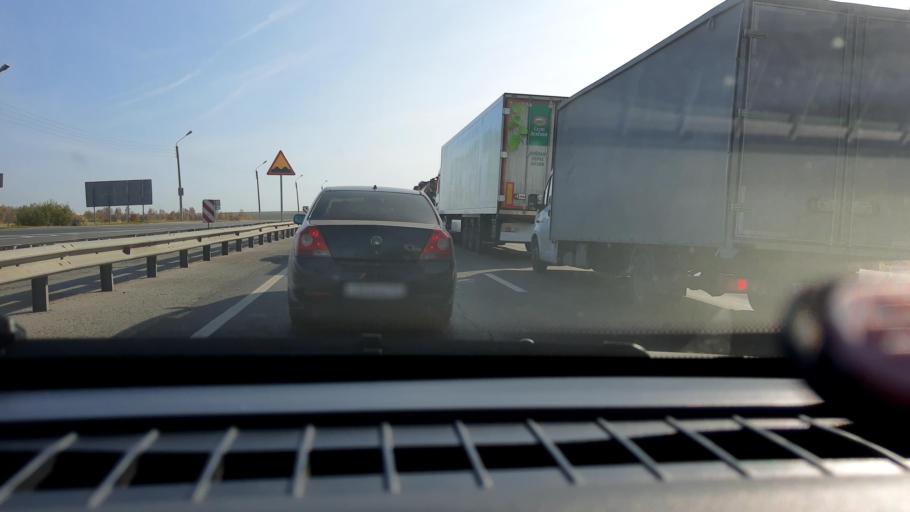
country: RU
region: Nizjnij Novgorod
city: Kstovo
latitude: 56.1257
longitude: 44.2647
